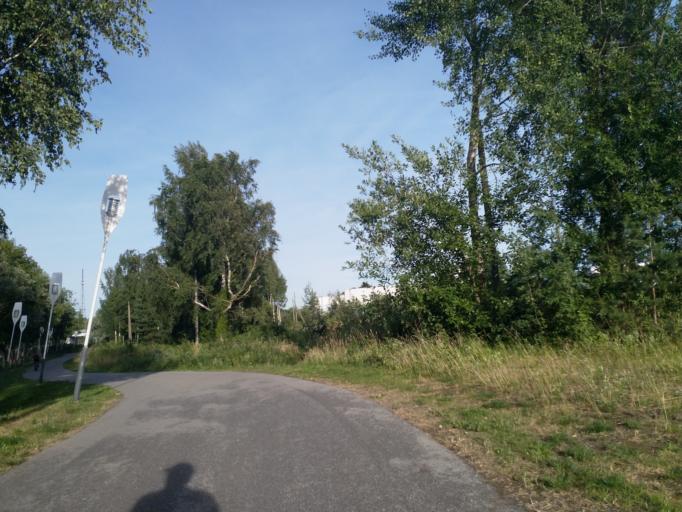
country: EE
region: Paernumaa
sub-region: Paernu linn
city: Parnu
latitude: 58.3775
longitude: 24.5479
